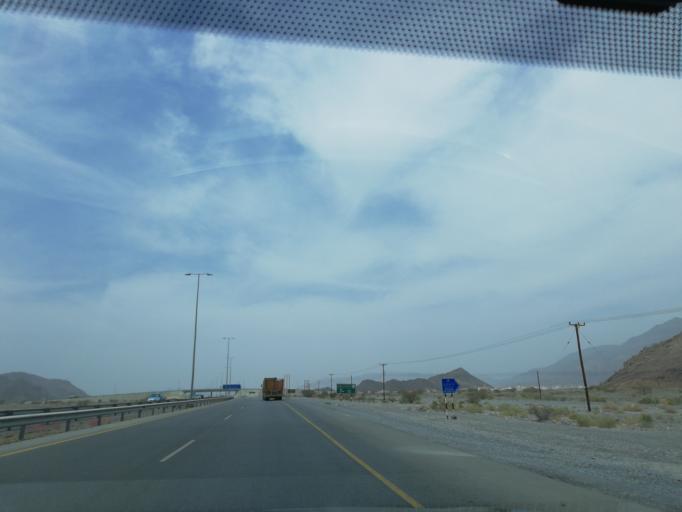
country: OM
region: Muhafazat ad Dakhiliyah
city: Izki
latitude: 22.8902
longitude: 57.6899
